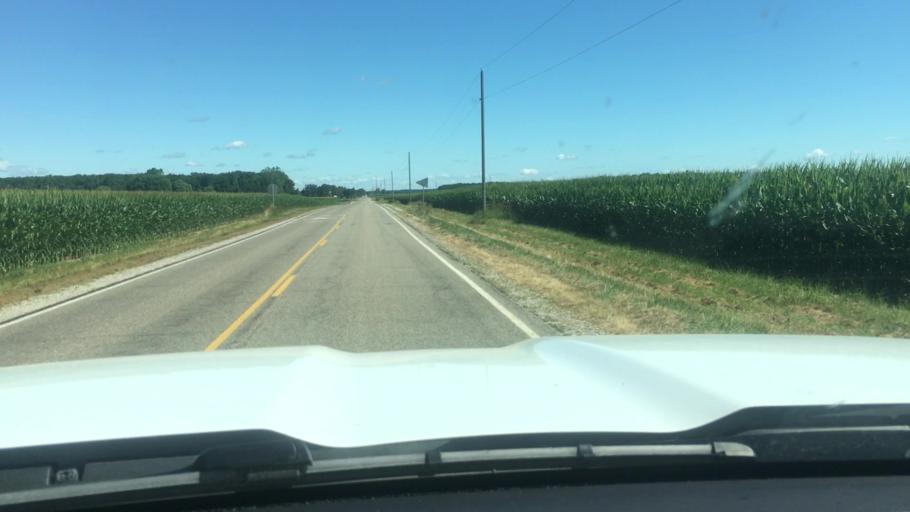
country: US
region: Michigan
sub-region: Montcalm County
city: Carson City
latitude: 43.1846
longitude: -84.7780
